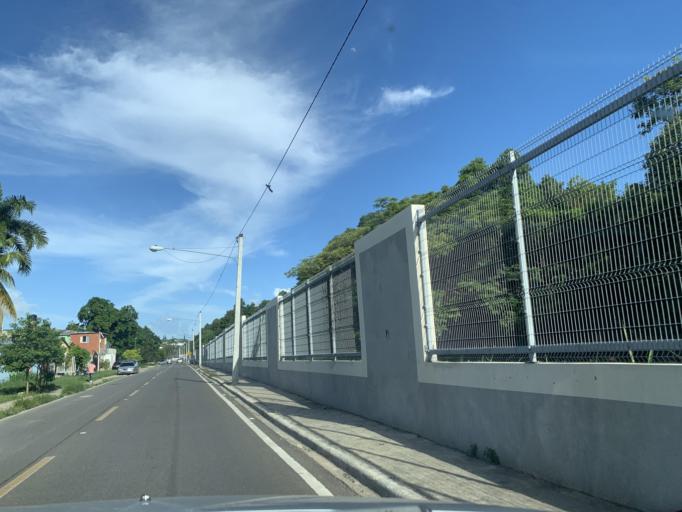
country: DO
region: Santiago
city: Santiago de los Caballeros
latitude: 19.4703
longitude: -70.6998
